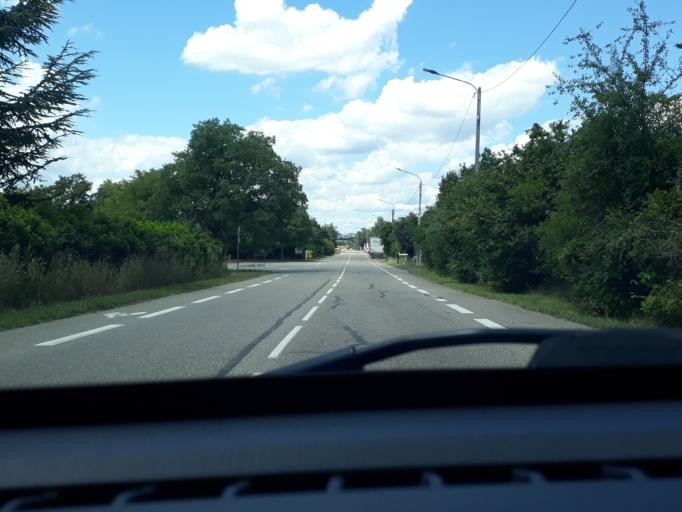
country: FR
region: Rhone-Alpes
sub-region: Departement du Rhone
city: Saint-Priest
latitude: 45.7095
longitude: 4.9269
